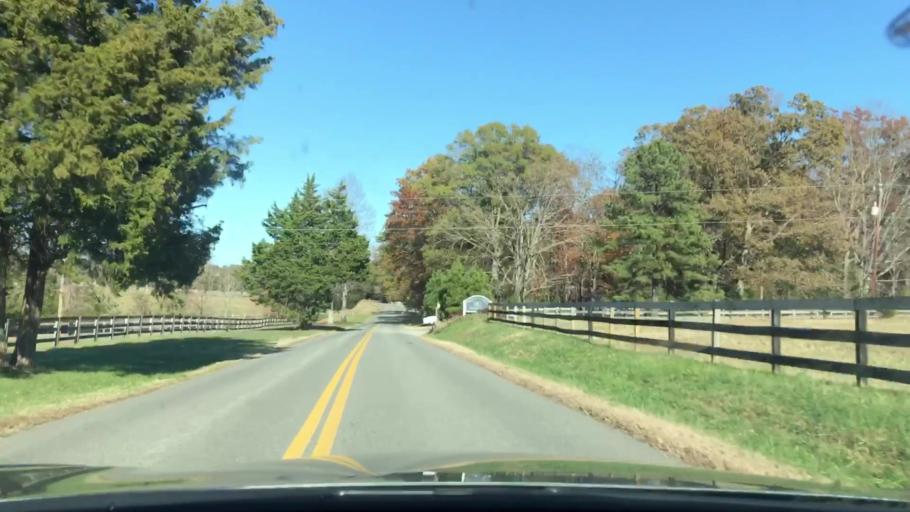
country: US
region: Virginia
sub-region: Henrico County
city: Short Pump
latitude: 37.6610
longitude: -77.7149
